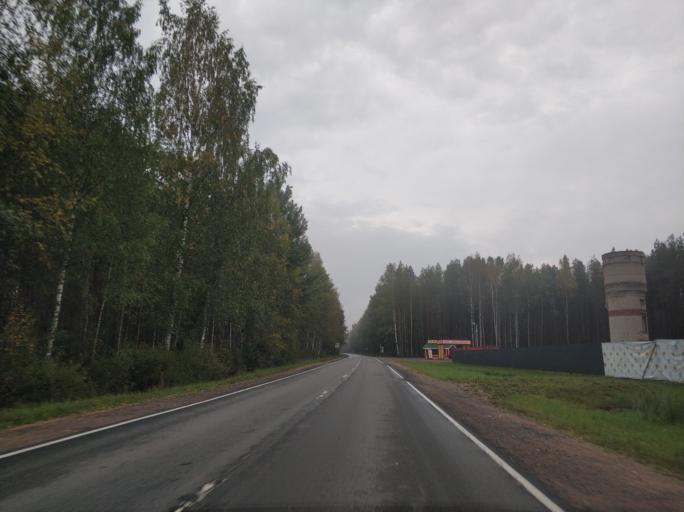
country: RU
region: Leningrad
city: Shcheglovo
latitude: 60.0926
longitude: 30.8539
